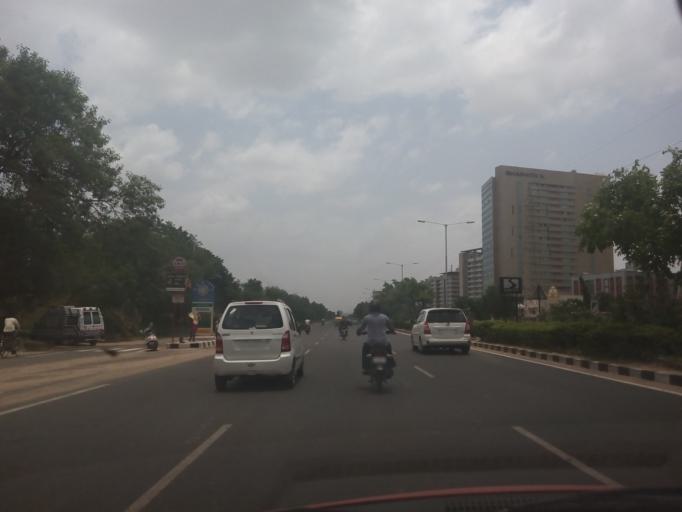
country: IN
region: Gujarat
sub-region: Ahmadabad
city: Sarkhej
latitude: 23.0120
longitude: 72.5025
